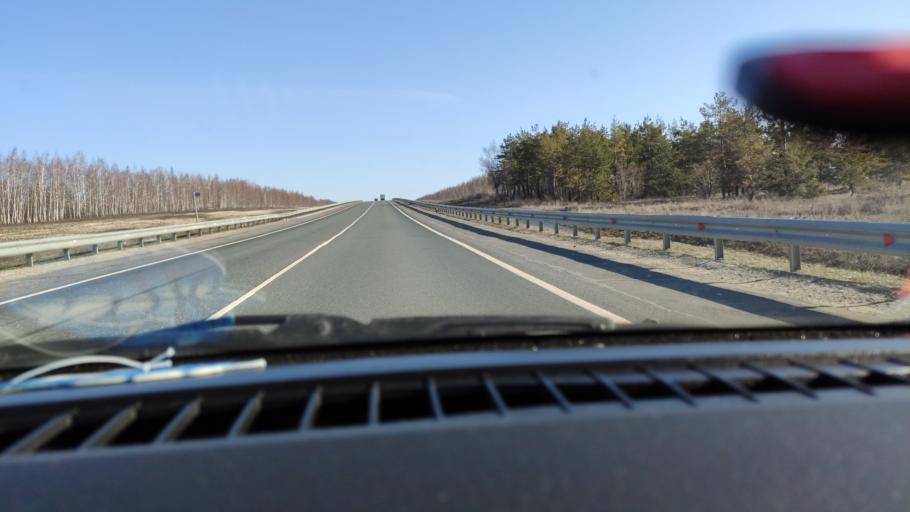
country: RU
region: Samara
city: Syzran'
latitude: 52.9023
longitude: 48.2971
